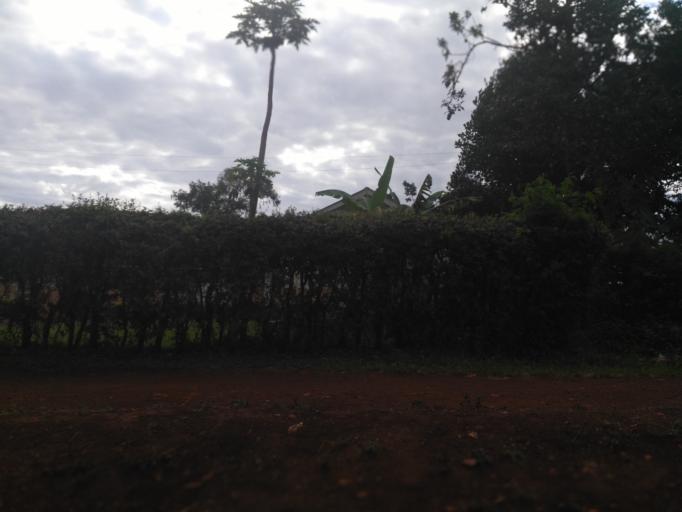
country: UG
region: Eastern Region
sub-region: Jinja District
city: Jinja
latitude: 0.4266
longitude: 33.1907
